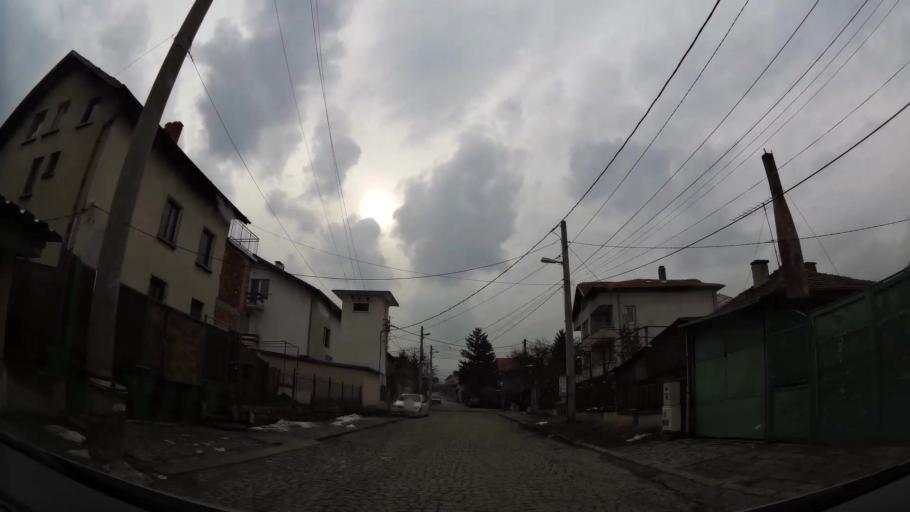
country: BG
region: Sofiya
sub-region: Obshtina Bozhurishte
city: Bozhurishte
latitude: 42.6971
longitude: 23.2259
